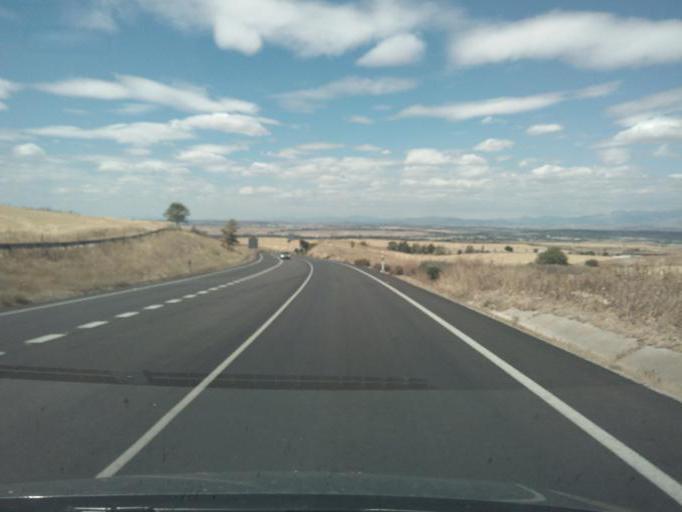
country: ES
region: Madrid
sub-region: Provincia de Madrid
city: Cobena
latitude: 40.5567
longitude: -3.5063
